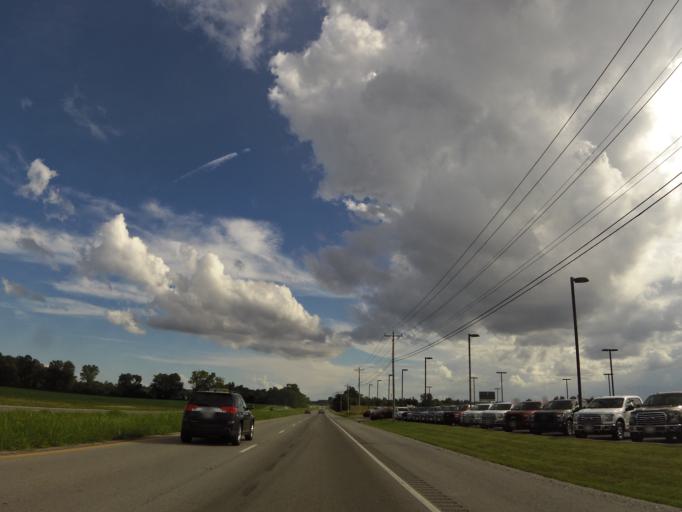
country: US
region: Kentucky
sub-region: Christian County
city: Hopkinsville
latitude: 36.8015
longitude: -87.4720
